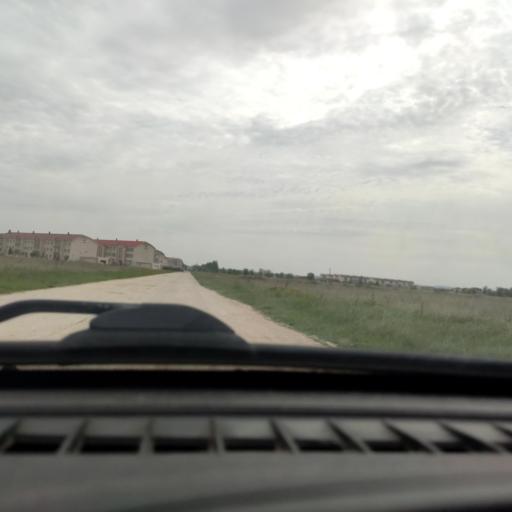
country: RU
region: Samara
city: Podstepki
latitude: 53.5281
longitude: 49.1730
